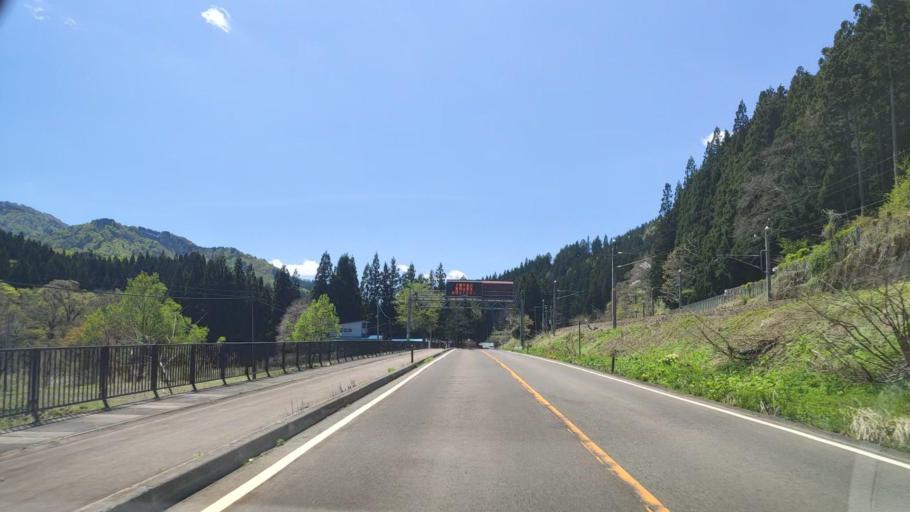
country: JP
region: Akita
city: Yuzawa
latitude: 39.0452
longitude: 140.3967
